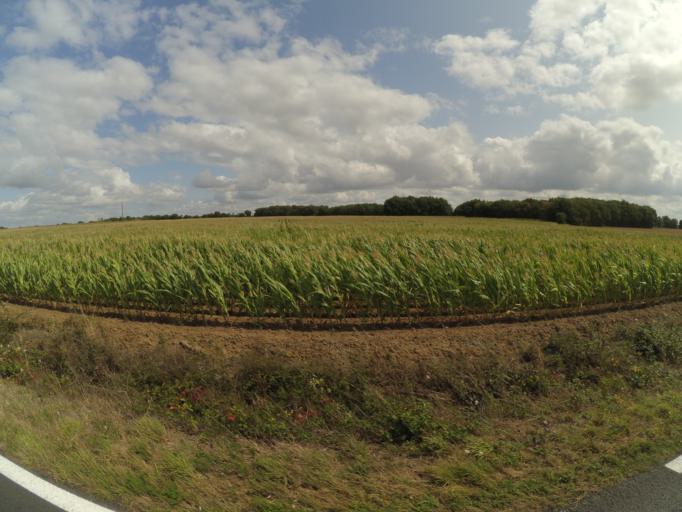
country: FR
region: Pays de la Loire
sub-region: Departement de la Vendee
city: La Bernardiere
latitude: 47.0134
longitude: -1.2777
